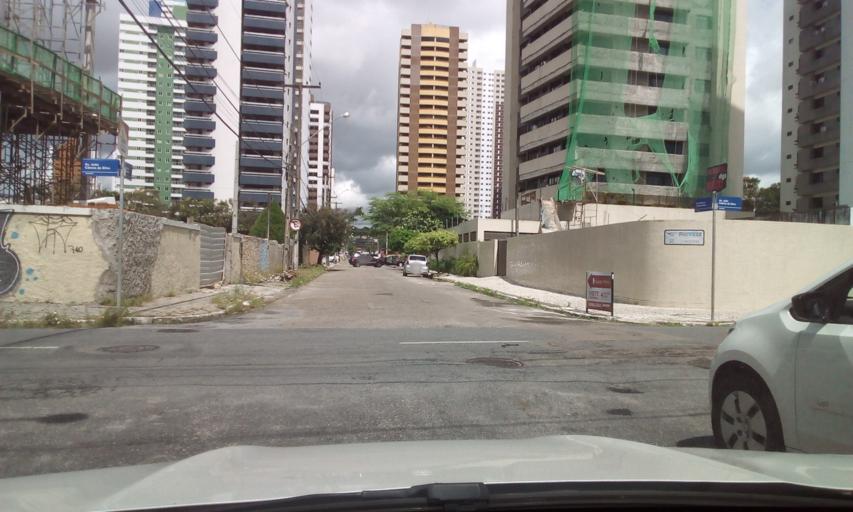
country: BR
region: Paraiba
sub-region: Joao Pessoa
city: Joao Pessoa
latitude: -7.1004
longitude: -34.8388
